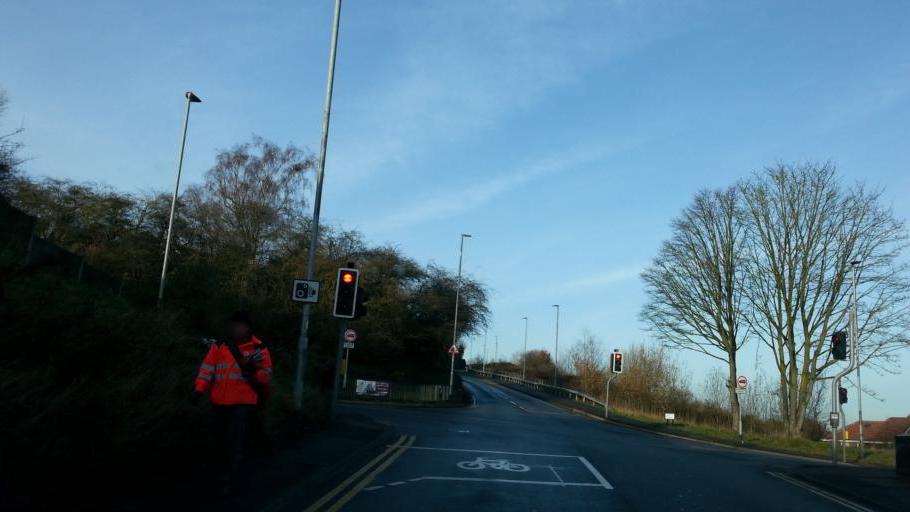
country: GB
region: England
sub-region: Stoke-on-Trent
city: Stoke-on-Trent
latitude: 53.0514
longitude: -2.1517
